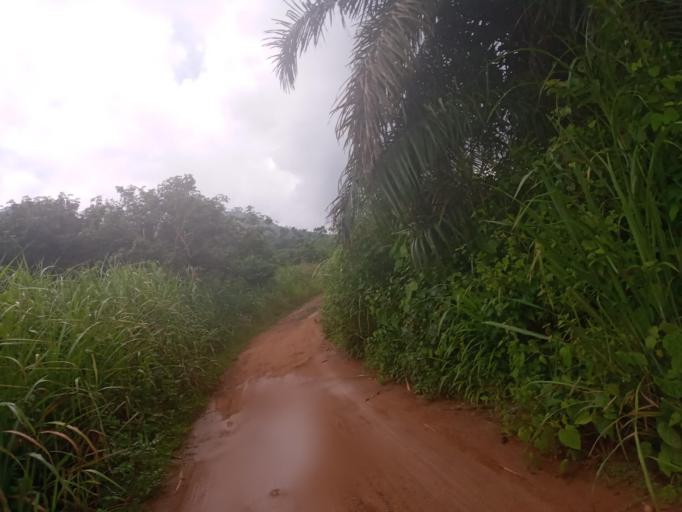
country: SL
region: Northern Province
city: Bumbuna
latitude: 8.9284
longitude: -11.7460
